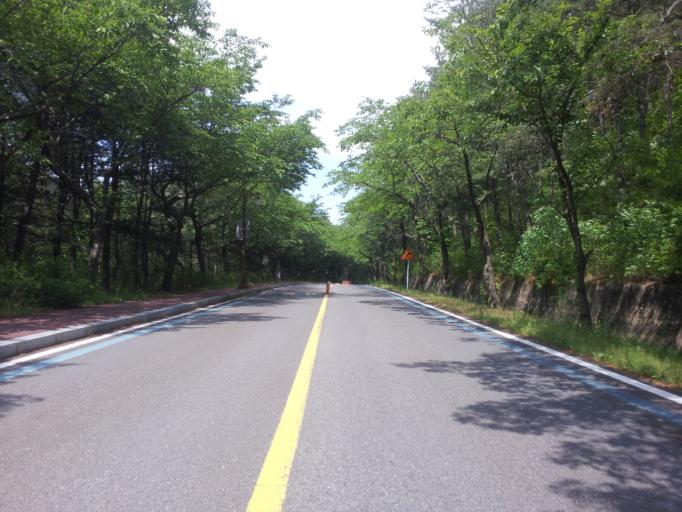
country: KR
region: Daejeon
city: Sintansin
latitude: 36.4736
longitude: 127.4777
